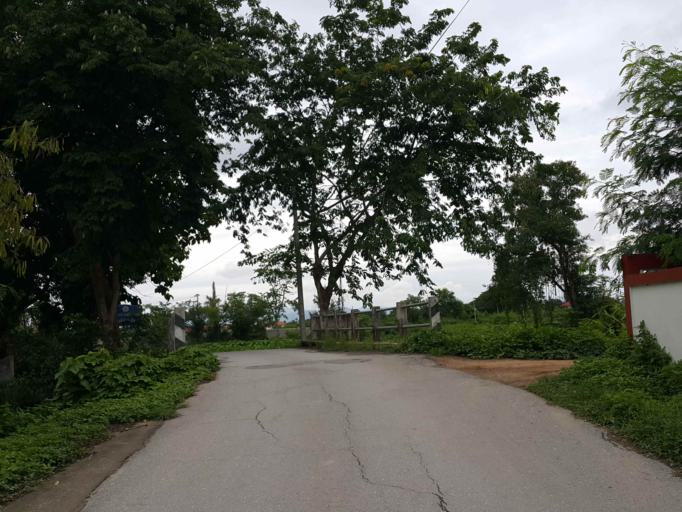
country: TH
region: Chiang Mai
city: San Sai
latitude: 18.8281
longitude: 99.0607
